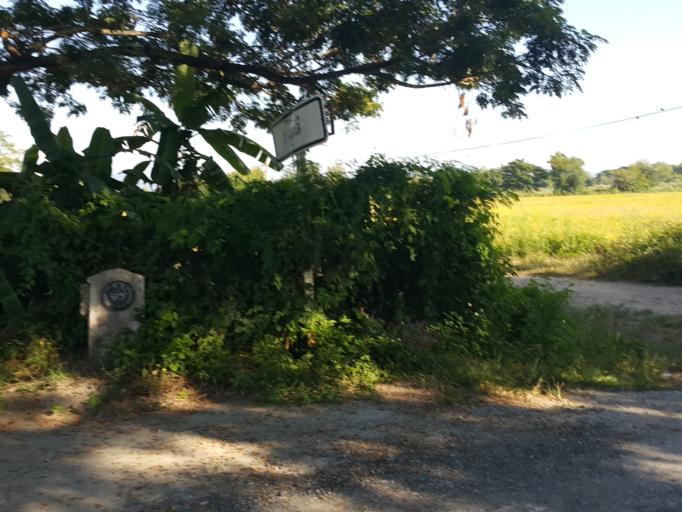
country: TH
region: Chiang Mai
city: San Kamphaeng
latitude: 18.8078
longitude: 99.1180
